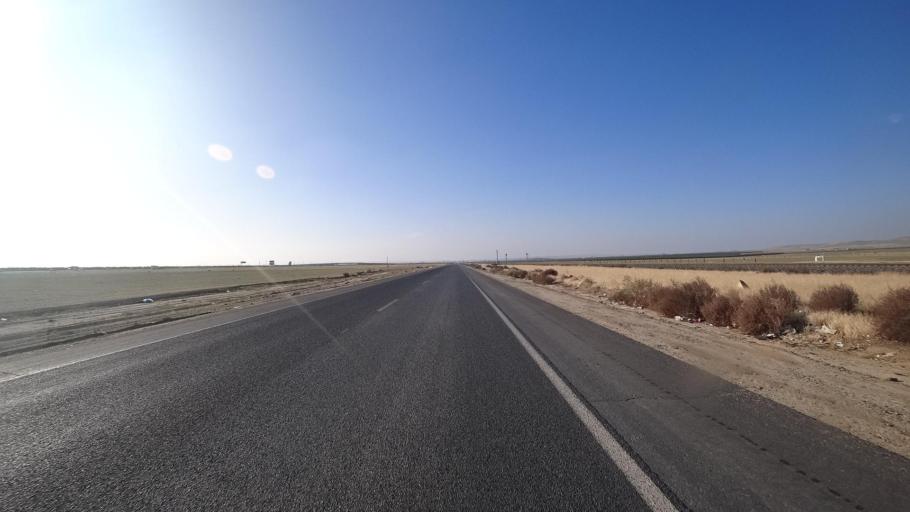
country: US
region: California
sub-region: Kern County
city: Lamont
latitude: 35.3341
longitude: -118.8140
